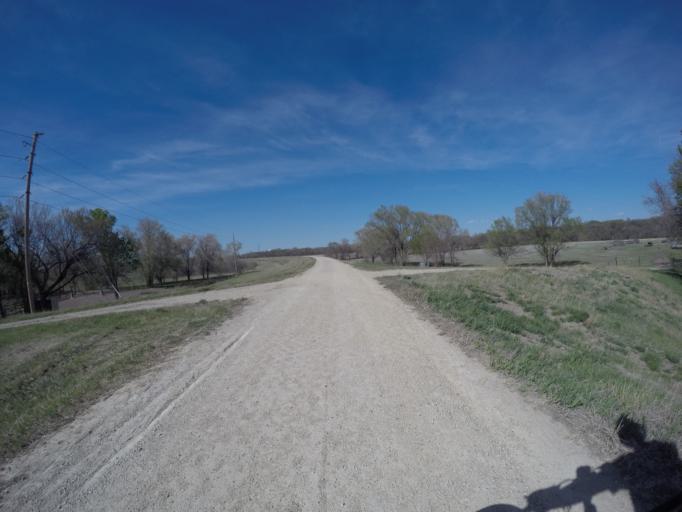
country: US
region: Kansas
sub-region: Saline County
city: Salina
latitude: 38.8143
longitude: -97.5828
